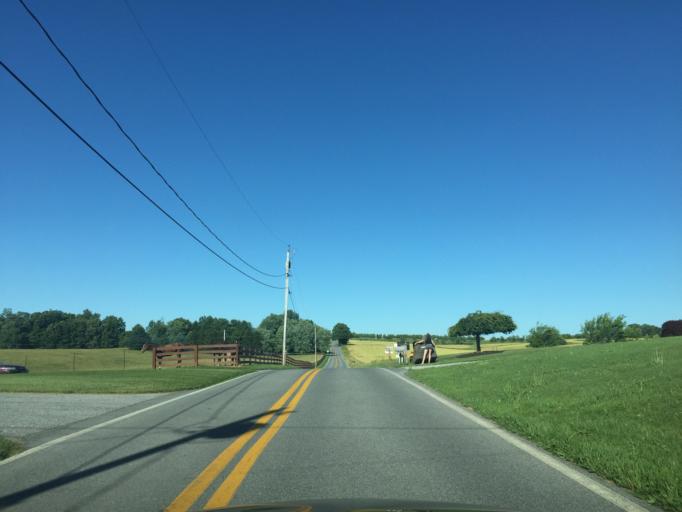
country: US
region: Maryland
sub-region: Carroll County
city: Hampstead
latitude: 39.5529
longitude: -76.8540
